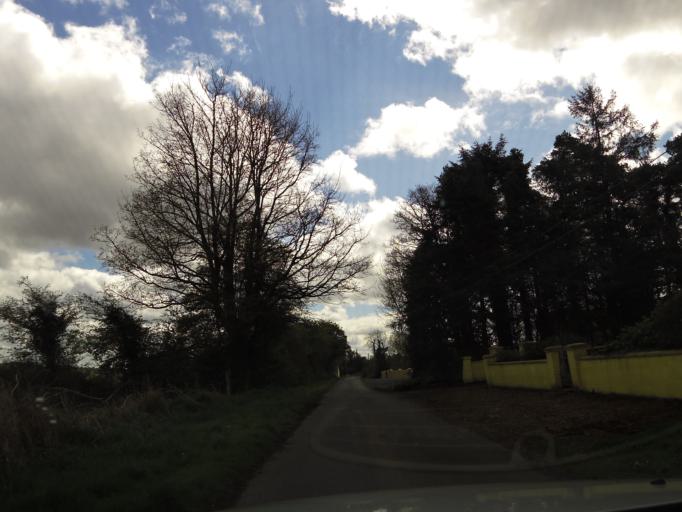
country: IE
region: Connaught
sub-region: Maigh Eo
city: Kiltamagh
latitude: 53.7921
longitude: -8.9639
